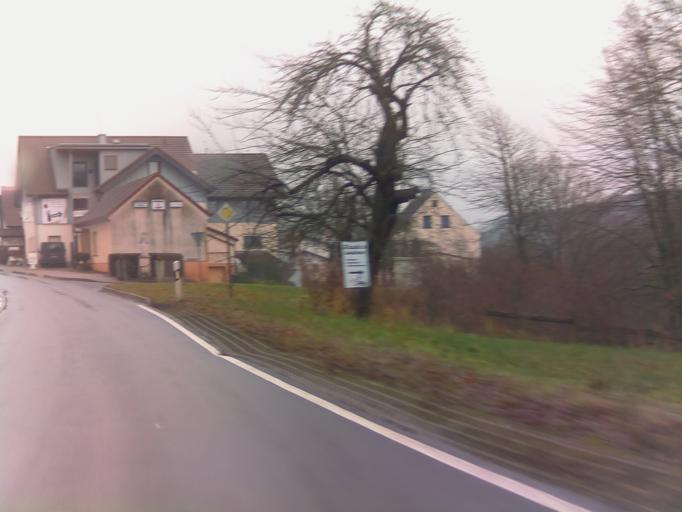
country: DE
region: Hesse
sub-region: Regierungsbezirk Kassel
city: Eichenzell
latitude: 50.4785
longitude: 9.7358
